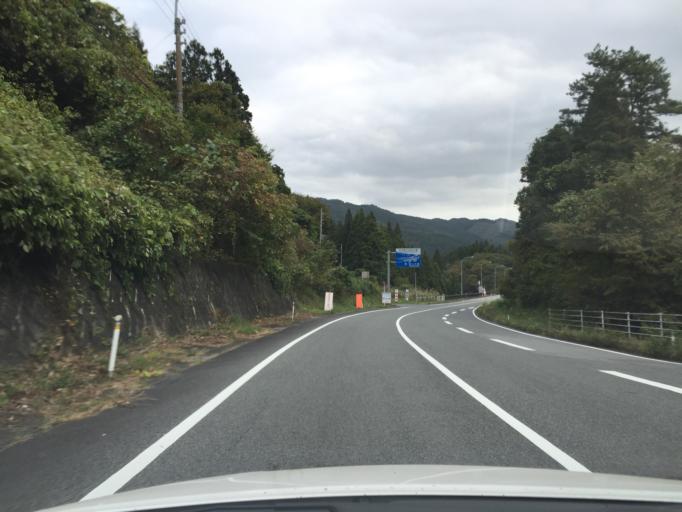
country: JP
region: Ibaraki
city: Kitaibaraki
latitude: 36.9341
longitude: 140.6825
